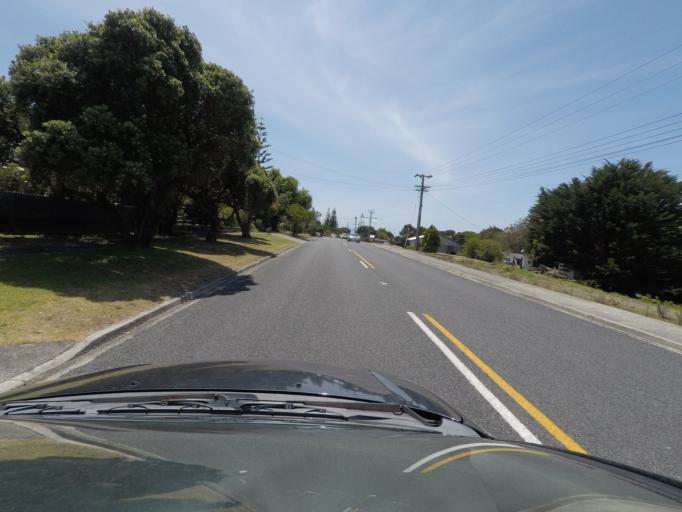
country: NZ
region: Auckland
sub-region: Auckland
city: Warkworth
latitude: -36.2938
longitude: 174.8014
